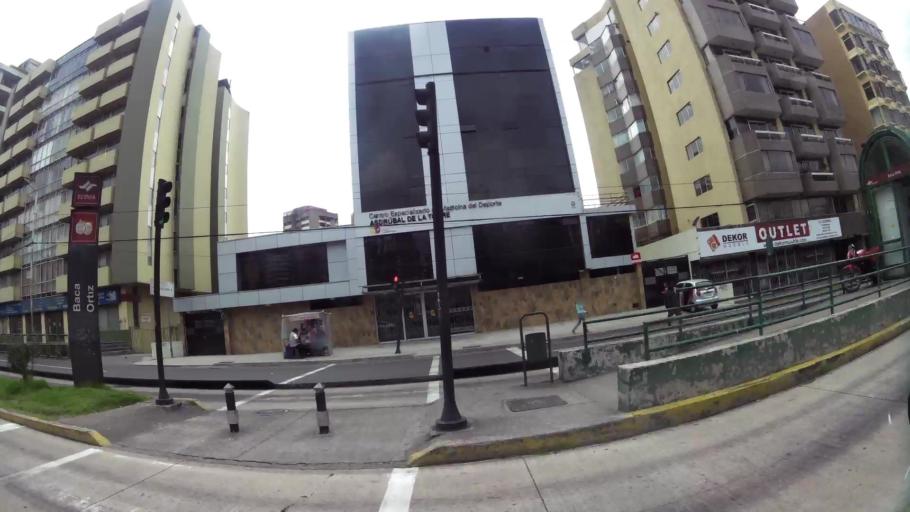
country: EC
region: Pichincha
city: Quito
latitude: -0.2022
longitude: -78.4867
